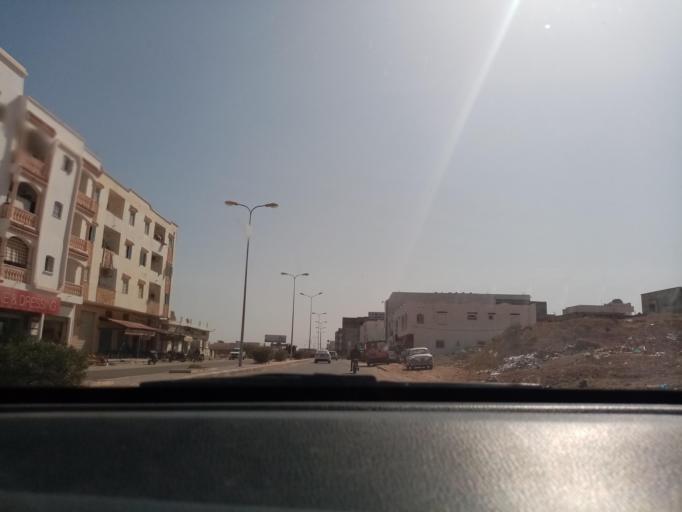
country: TN
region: Qabis
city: Gabes
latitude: 33.8520
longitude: 10.1090
